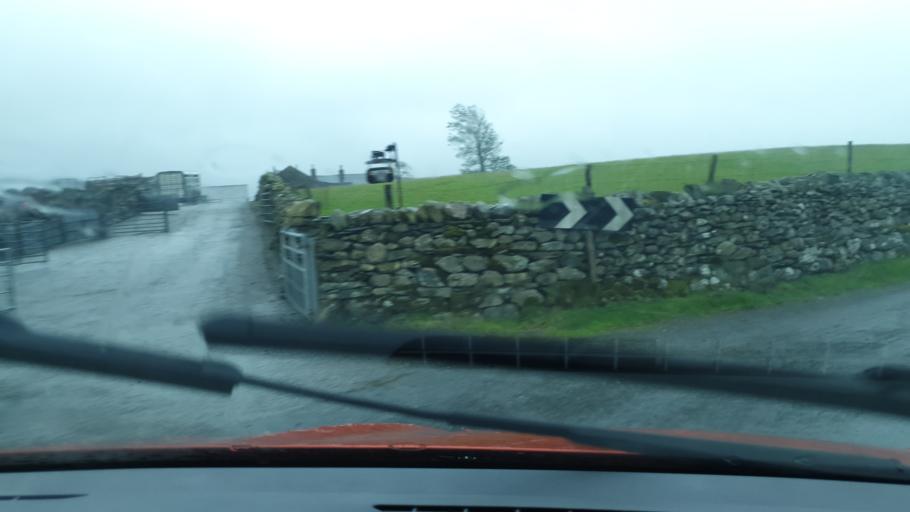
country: GB
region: England
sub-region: Cumbria
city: Millom
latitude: 54.3446
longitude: -3.2489
